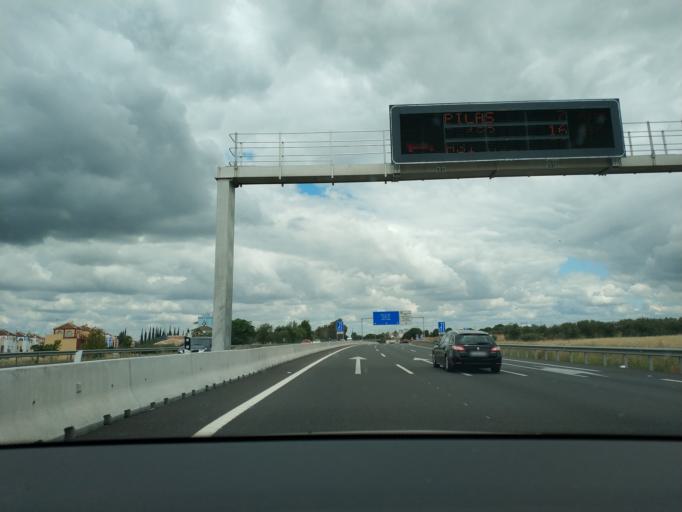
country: ES
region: Andalusia
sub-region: Provincia de Sevilla
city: Benacazon
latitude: 37.3590
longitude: -6.1935
